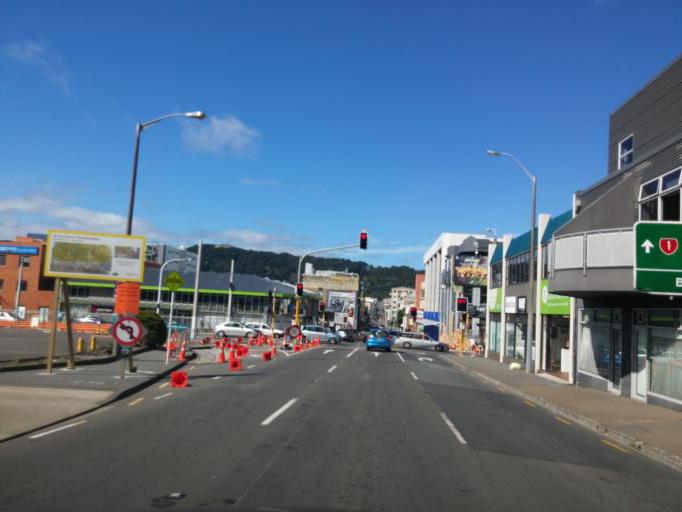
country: NZ
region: Wellington
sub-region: Wellington City
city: Wellington
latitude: -41.2940
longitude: 174.7724
